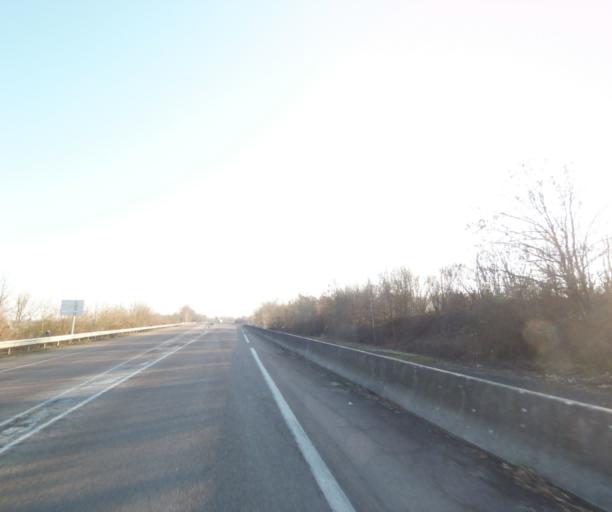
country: FR
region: Champagne-Ardenne
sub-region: Departement de la Haute-Marne
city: Chevillon
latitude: 48.5357
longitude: 5.0896
